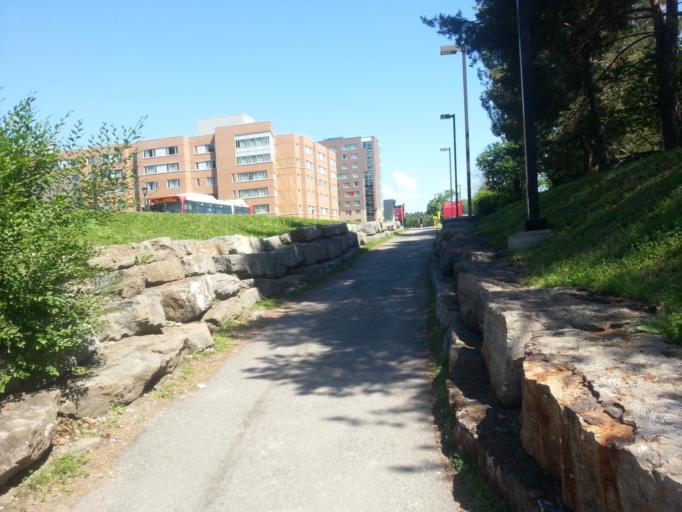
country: CA
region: Ontario
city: Ottawa
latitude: 45.3849
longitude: -75.6961
